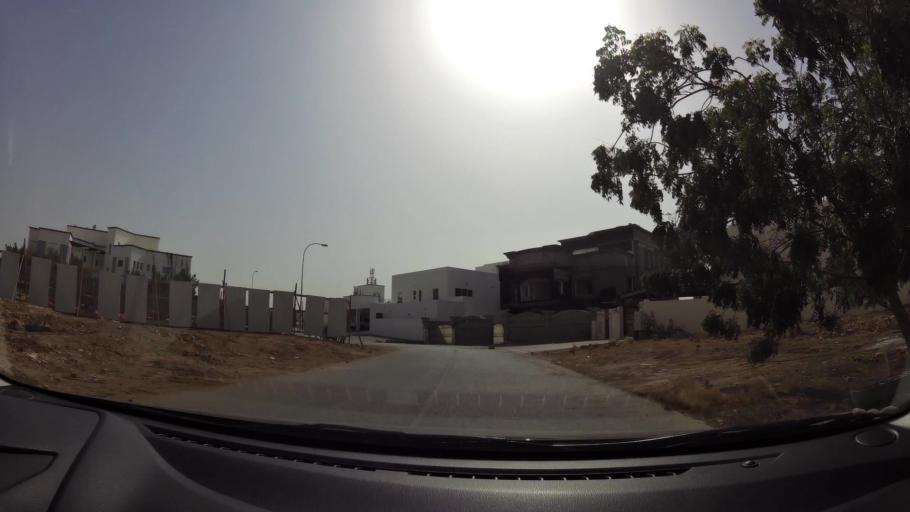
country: OM
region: Muhafazat Masqat
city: Bawshar
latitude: 23.5538
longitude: 58.3526
